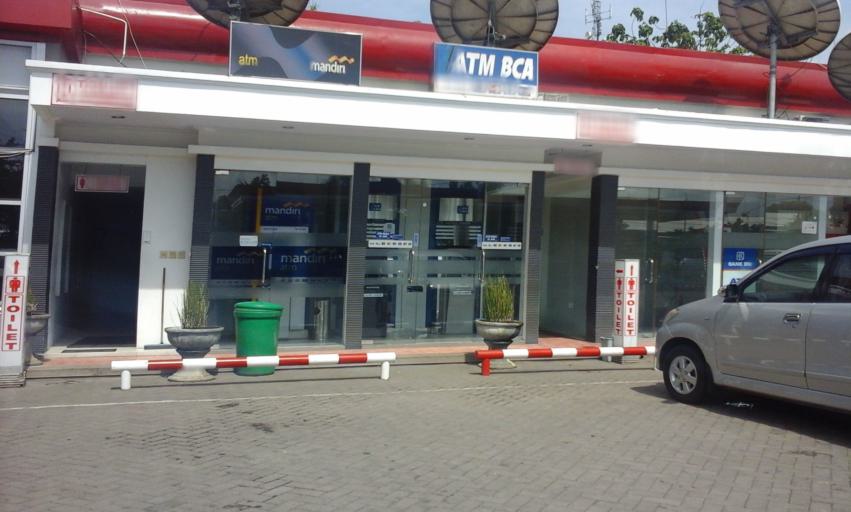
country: ID
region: East Java
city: Klatakan
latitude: -8.1523
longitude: 114.3963
